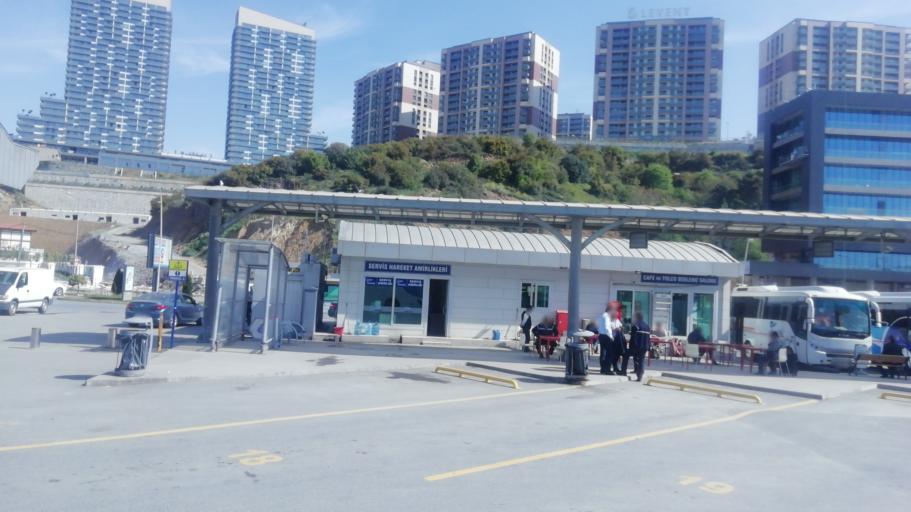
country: TR
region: Istanbul
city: Sisli
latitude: 41.0876
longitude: 28.9458
